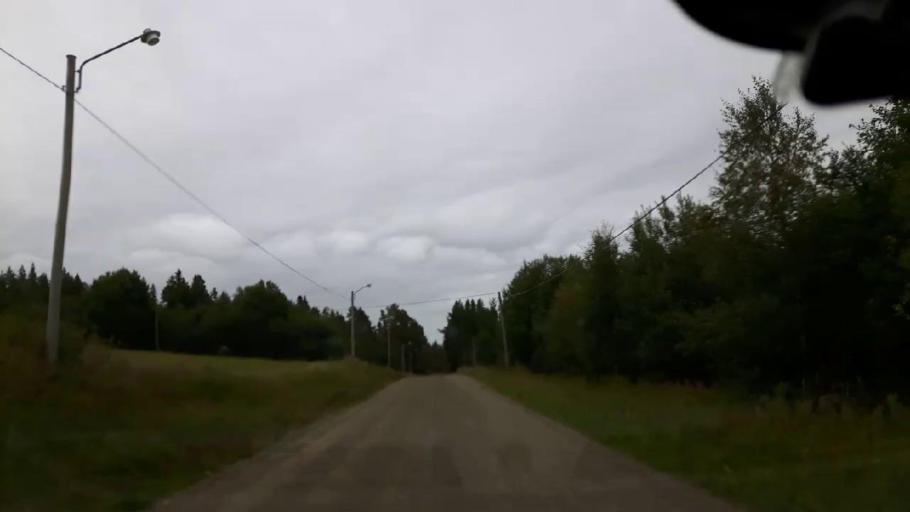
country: SE
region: Jaemtland
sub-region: Braecke Kommun
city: Braecke
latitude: 63.0318
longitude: 15.3694
